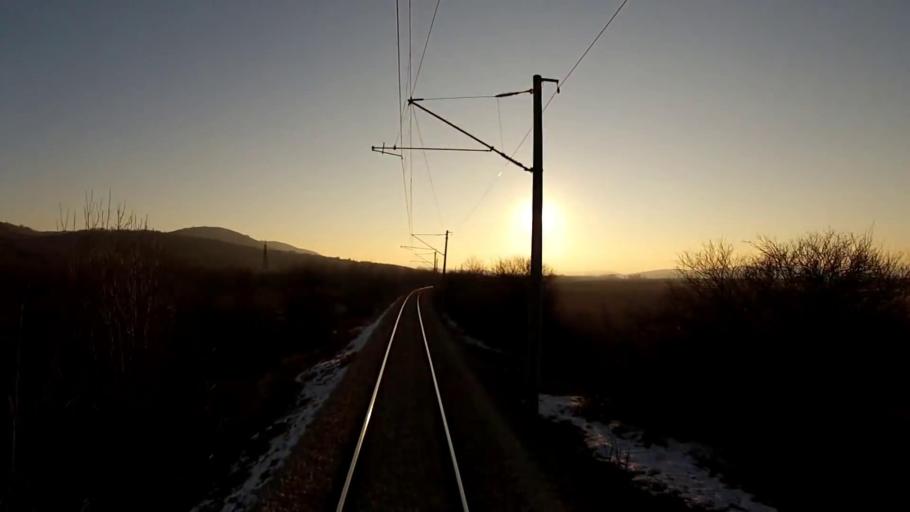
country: BG
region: Sofiya
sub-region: Obshtina Dragoman
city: Dragoman
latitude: 42.8952
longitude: 22.9672
